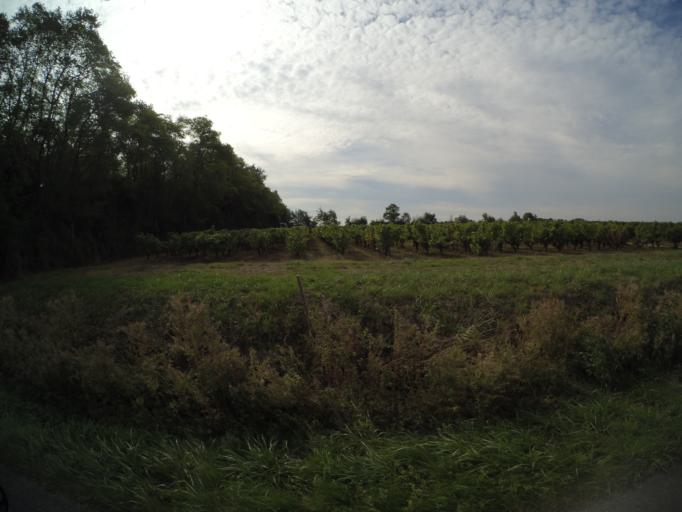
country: FR
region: Pays de la Loire
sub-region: Departement de Maine-et-Loire
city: Saint-Jean
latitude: 47.1952
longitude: -0.3556
